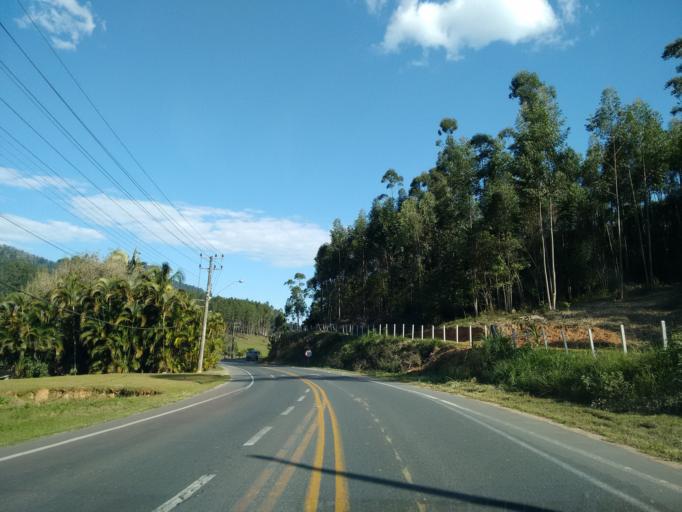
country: BR
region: Santa Catarina
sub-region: Timbo
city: Timbo
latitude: -26.7983
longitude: -49.2410
